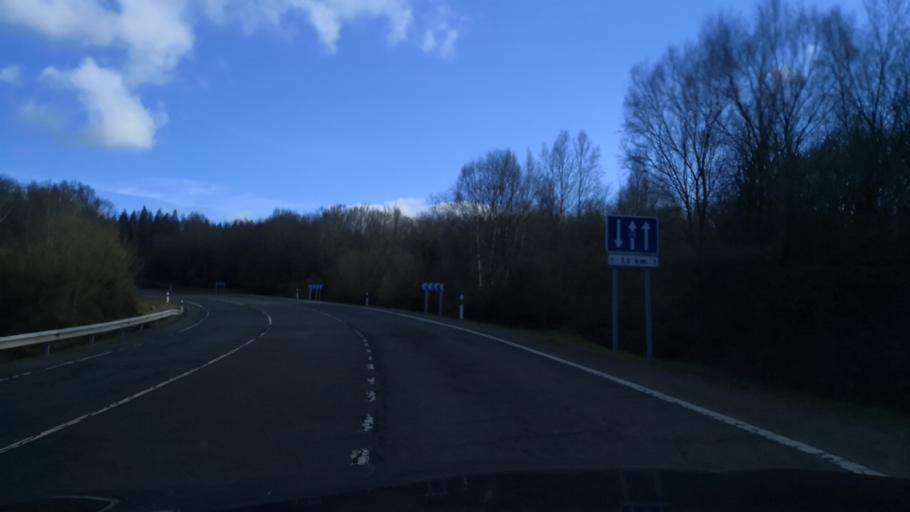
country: ES
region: Galicia
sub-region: Provincia da Coruna
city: Ribeira
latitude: 42.7116
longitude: -8.3584
